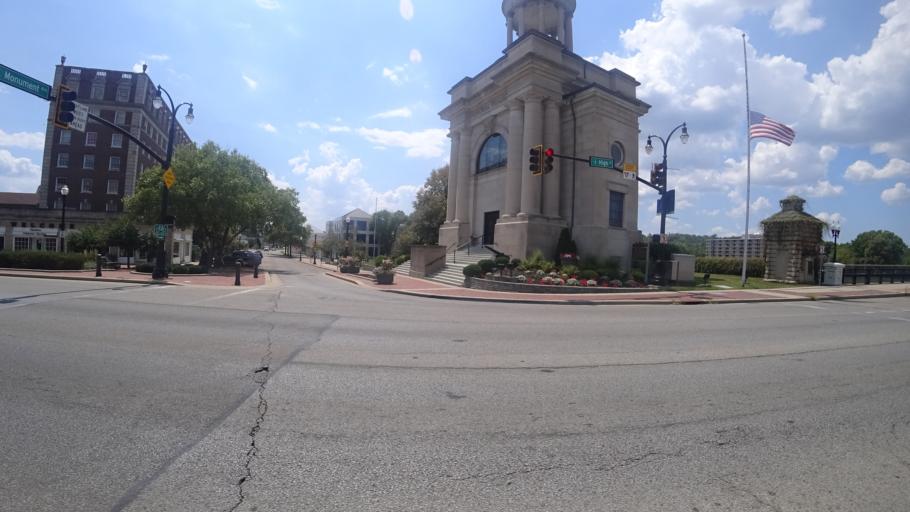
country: US
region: Ohio
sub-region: Butler County
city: Hamilton
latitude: 39.4007
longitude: -84.5645
